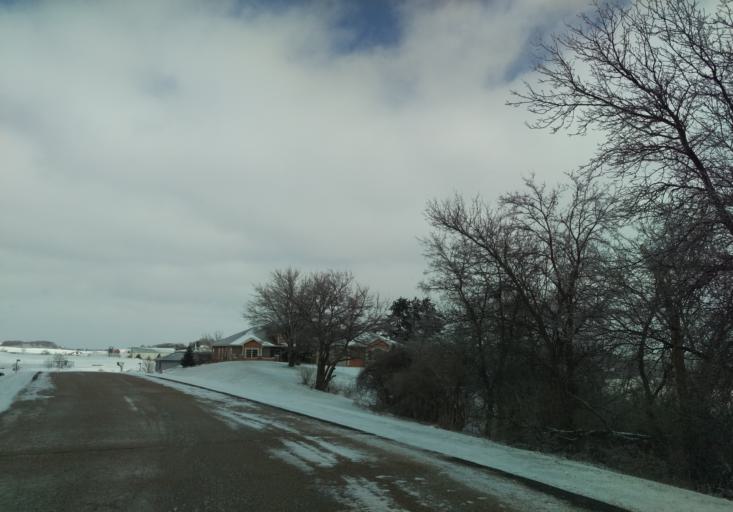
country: US
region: Wisconsin
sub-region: Dane County
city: Middleton
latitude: 43.1158
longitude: -89.5177
